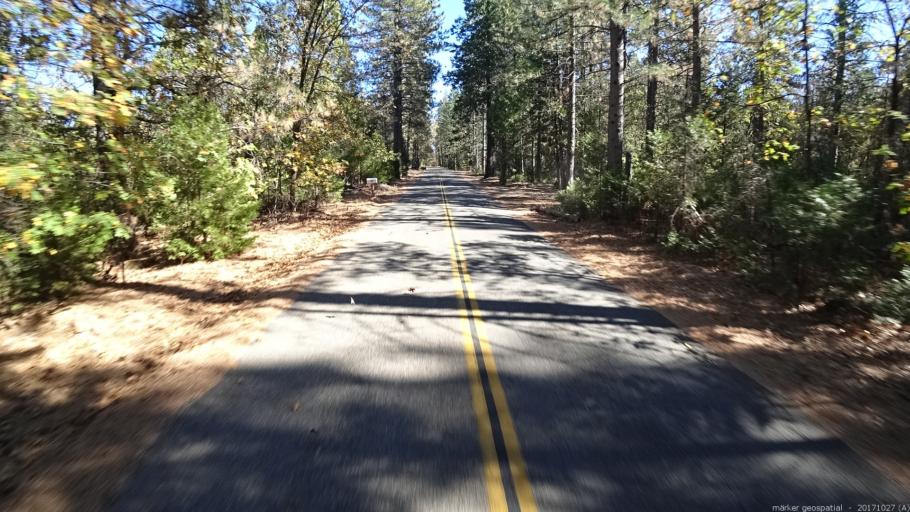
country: US
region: California
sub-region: Shasta County
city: Bella Vista
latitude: 40.7215
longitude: -122.0125
